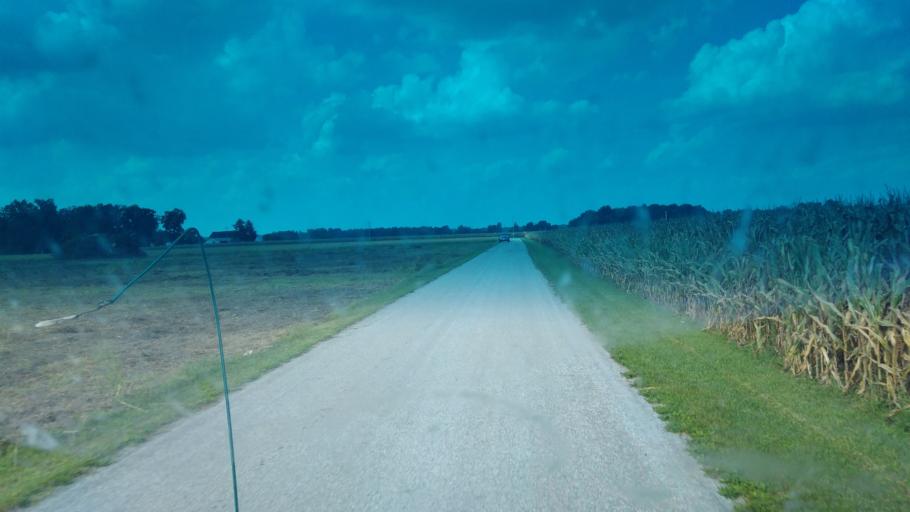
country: US
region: Ohio
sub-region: Hardin County
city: Kenton
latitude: 40.7289
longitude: -83.6144
